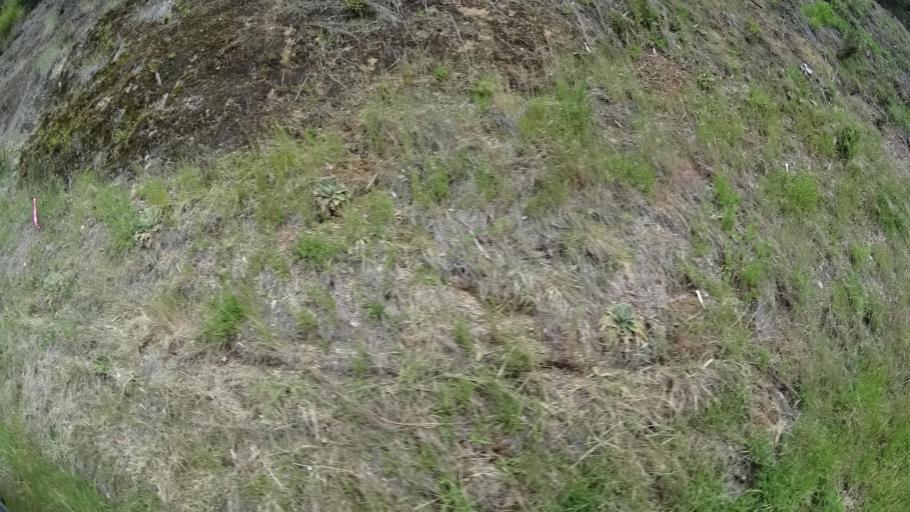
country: US
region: California
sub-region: Humboldt County
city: Blue Lake
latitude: 40.7630
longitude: -123.9217
